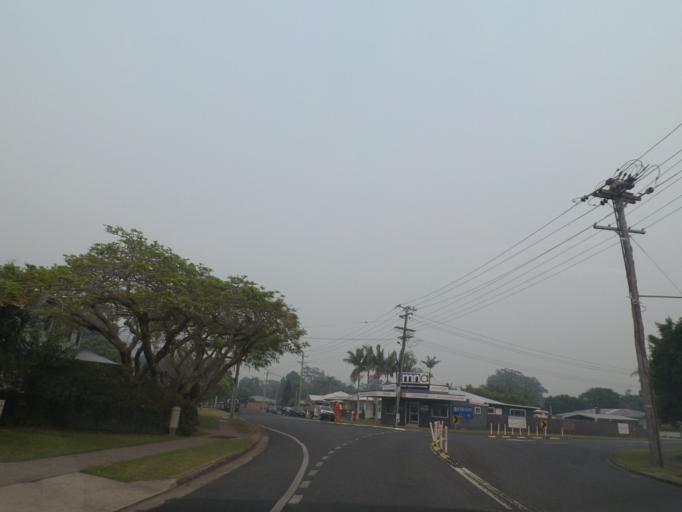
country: AU
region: New South Wales
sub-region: Coffs Harbour
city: Coffs Harbour
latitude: -30.2925
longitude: 153.1079
